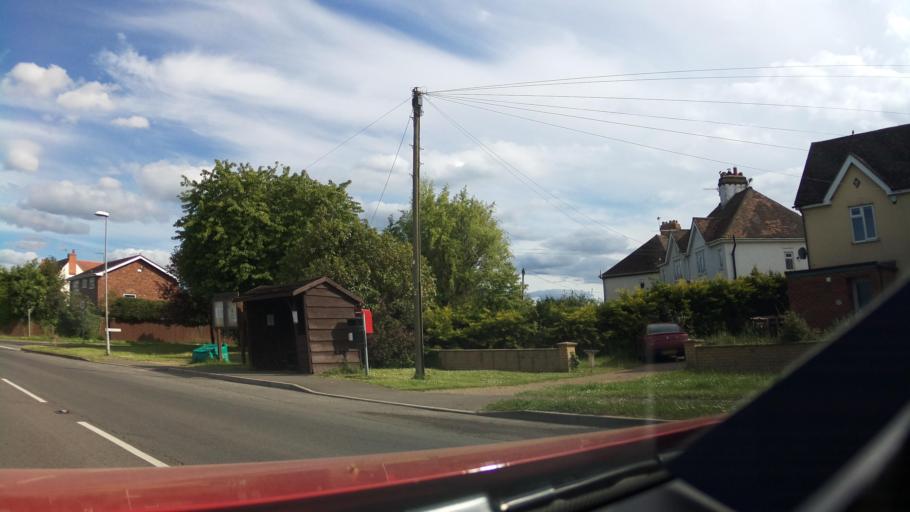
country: GB
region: England
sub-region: Worcestershire
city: Badsey
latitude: 52.0853
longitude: -1.8567
